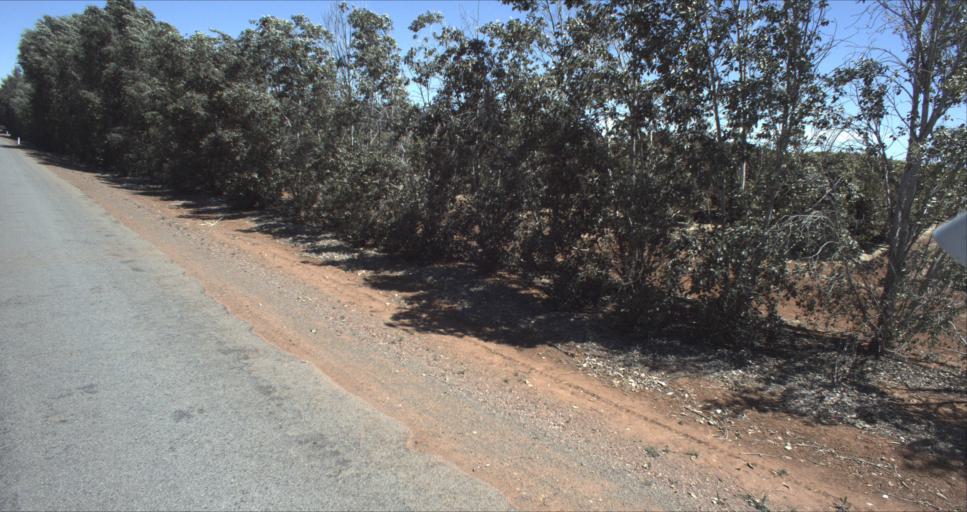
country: AU
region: New South Wales
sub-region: Leeton
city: Leeton
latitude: -34.5266
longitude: 146.3298
